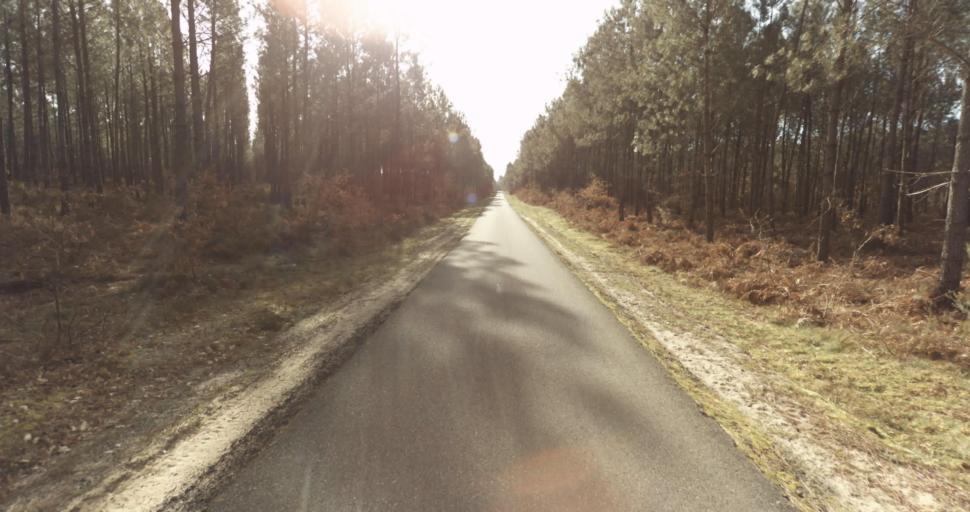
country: FR
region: Aquitaine
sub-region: Departement des Landes
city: Roquefort
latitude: 44.0730
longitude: -0.2667
